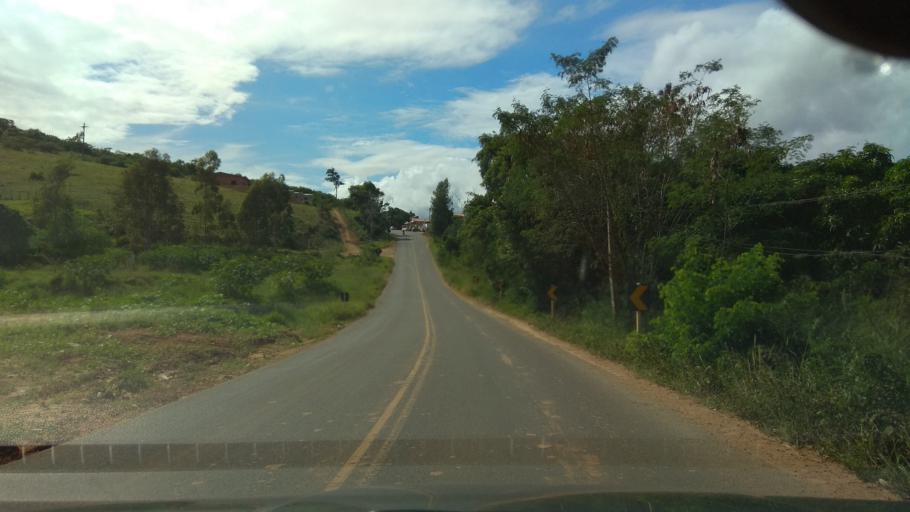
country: BR
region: Bahia
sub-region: Ubaira
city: Ubaira
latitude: -13.2712
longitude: -39.6564
